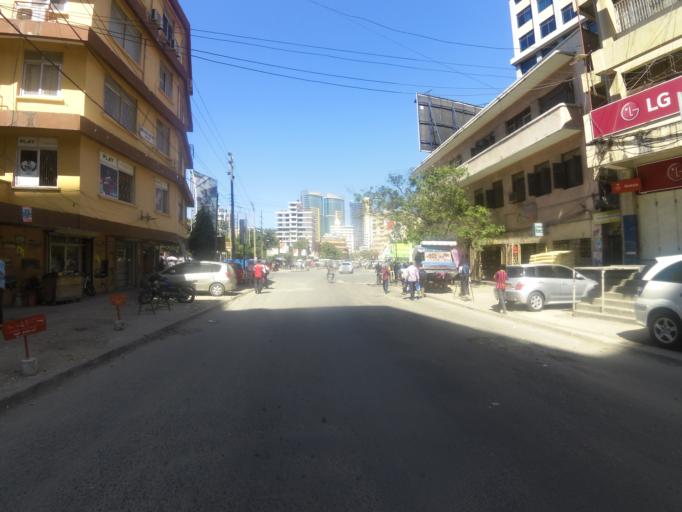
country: TZ
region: Dar es Salaam
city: Dar es Salaam
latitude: -6.8214
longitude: 39.2795
